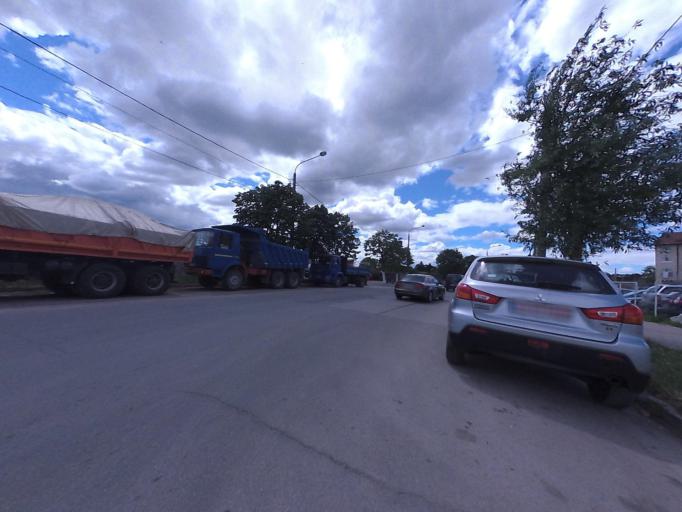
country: RO
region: Vaslui
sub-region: Municipiul Barlad
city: Barlad
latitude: 46.2131
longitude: 27.6663
